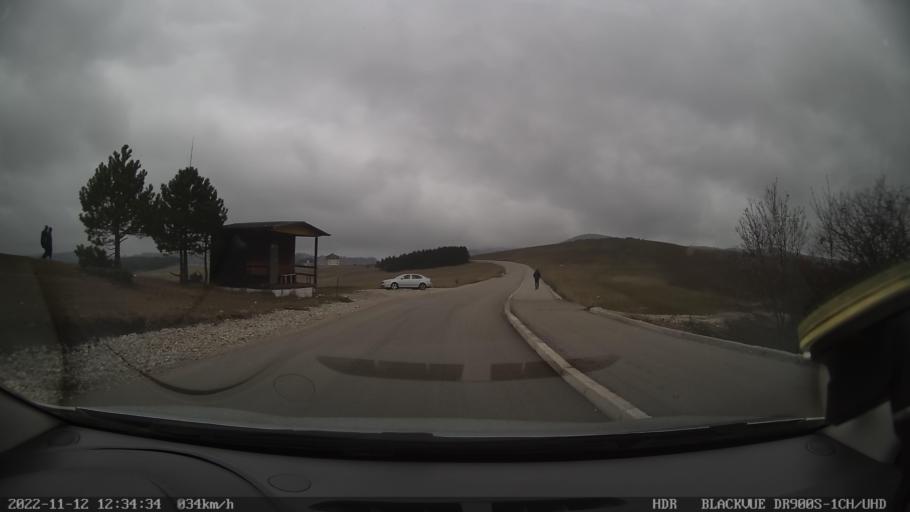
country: RS
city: Zlatibor
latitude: 43.7126
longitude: 19.7154
